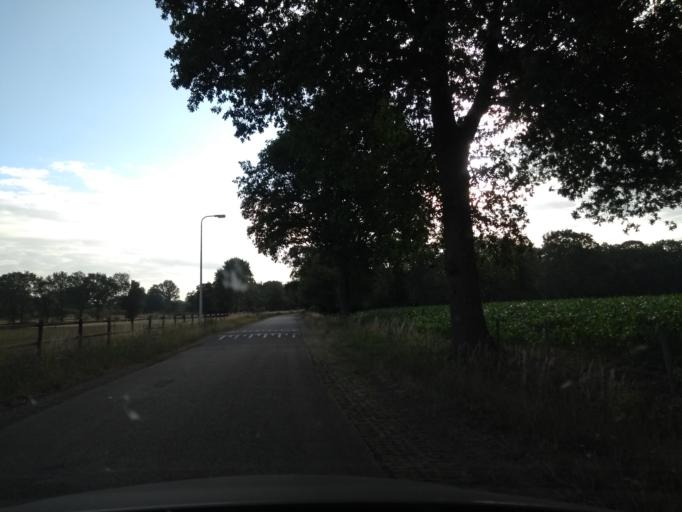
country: NL
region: Overijssel
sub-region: Gemeente Hof van Twente
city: Markelo
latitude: 52.2623
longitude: 6.4639
